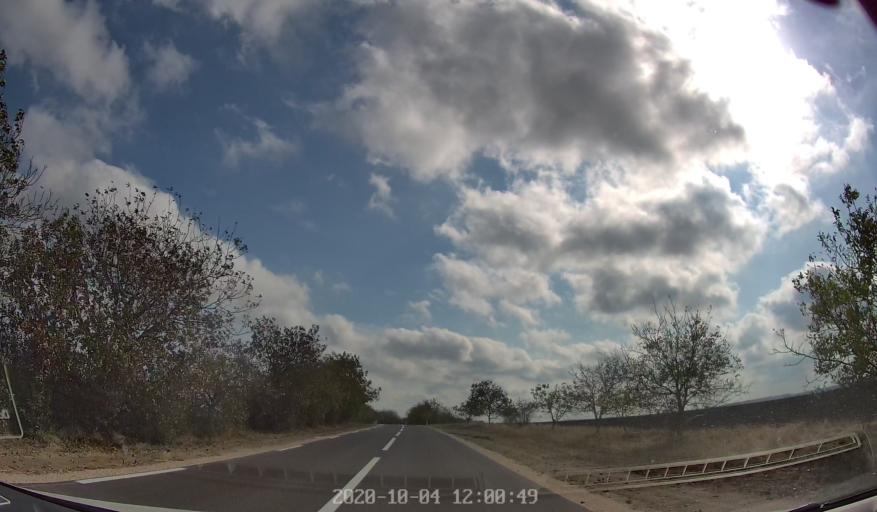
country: MD
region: Rezina
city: Saharna
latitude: 47.6297
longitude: 28.8788
